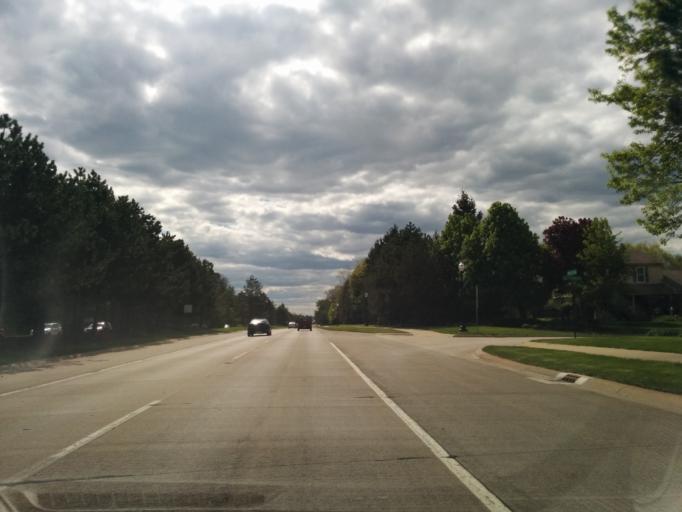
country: US
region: Michigan
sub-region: Oakland County
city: Farmington Hills
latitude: 42.4980
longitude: -83.4035
